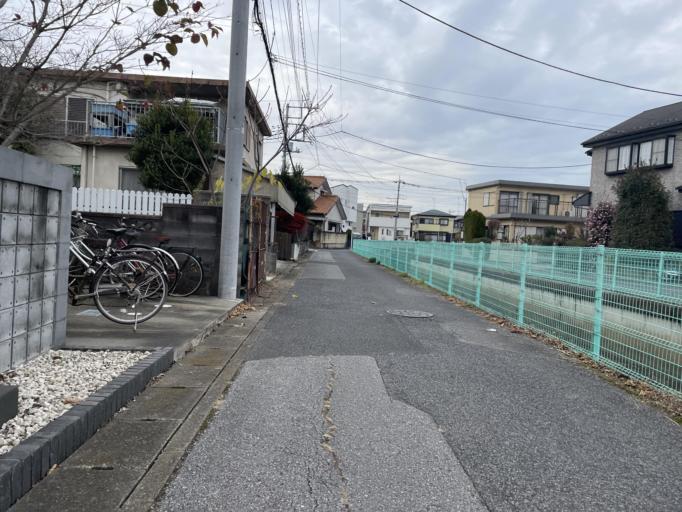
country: JP
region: Saitama
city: Shiraoka
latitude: 35.9969
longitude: 139.6530
